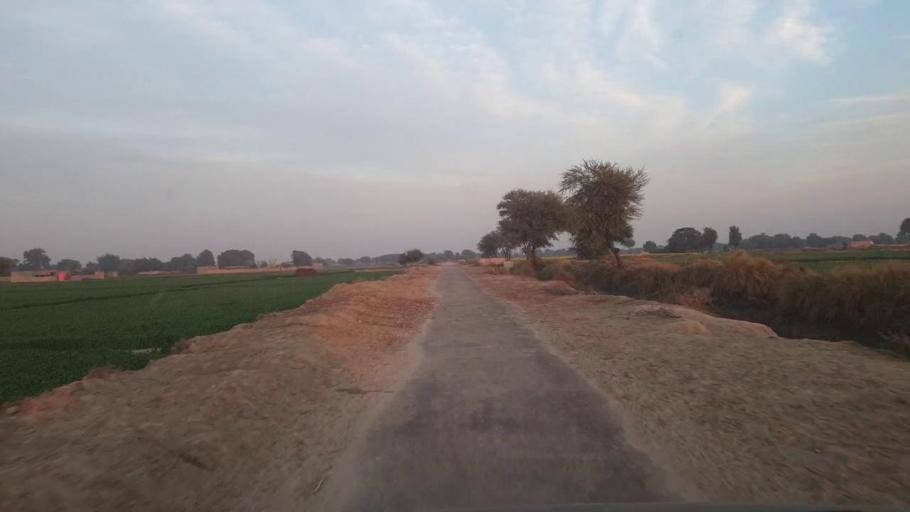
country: PK
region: Sindh
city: Shahpur Chakar
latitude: 26.0719
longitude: 68.5280
